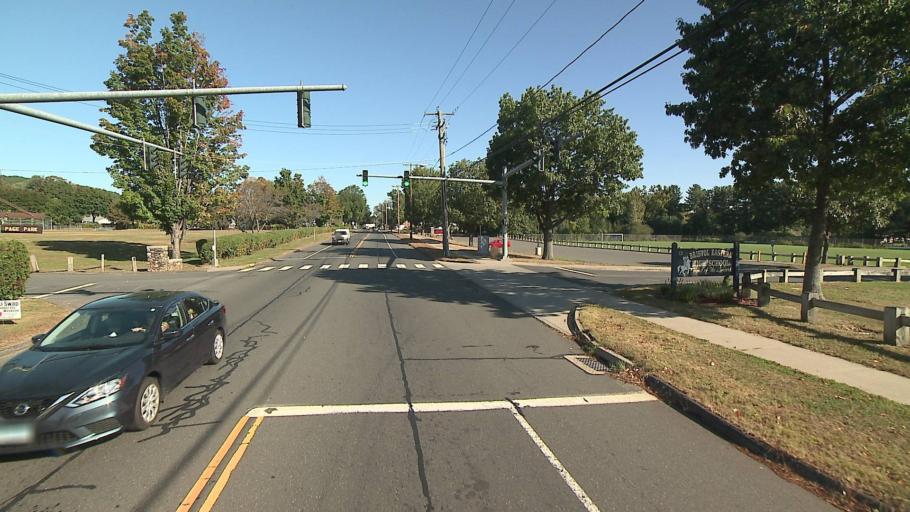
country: US
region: Connecticut
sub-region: Hartford County
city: Bristol
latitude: 41.6856
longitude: -72.9251
